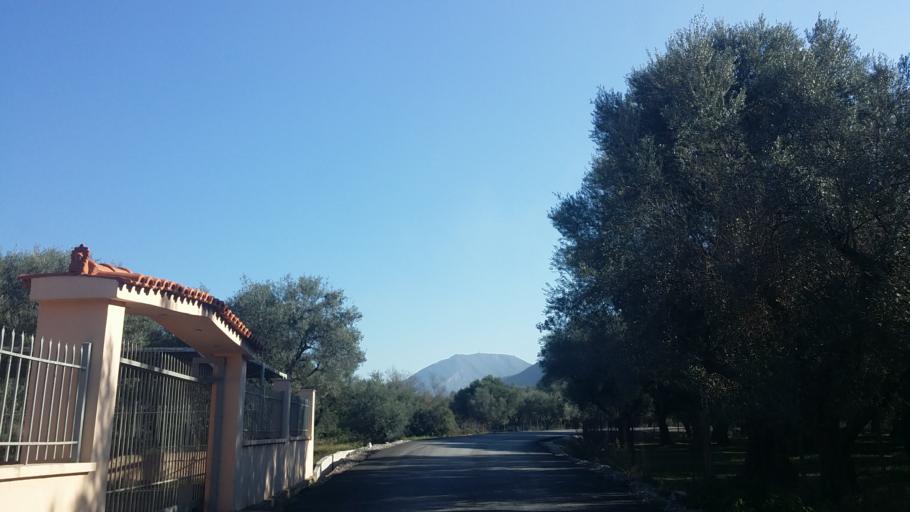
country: GR
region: West Greece
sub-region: Nomos Achaias
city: Temeni
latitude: 38.1942
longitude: 22.1840
